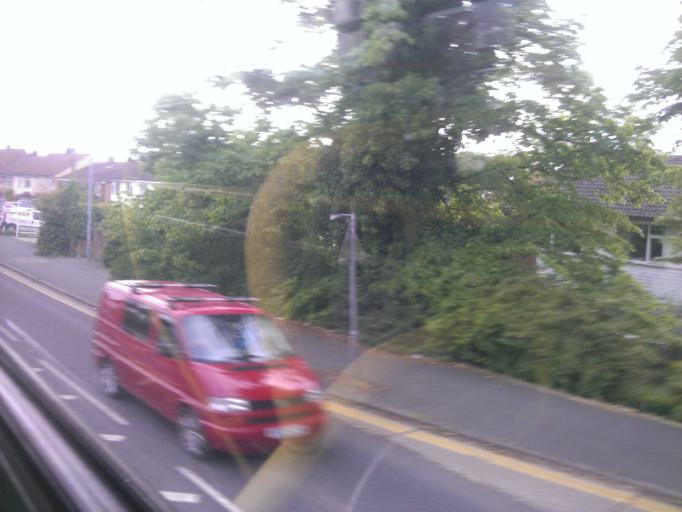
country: GB
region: England
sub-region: Essex
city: Colchester
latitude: 51.8968
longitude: 0.9191
